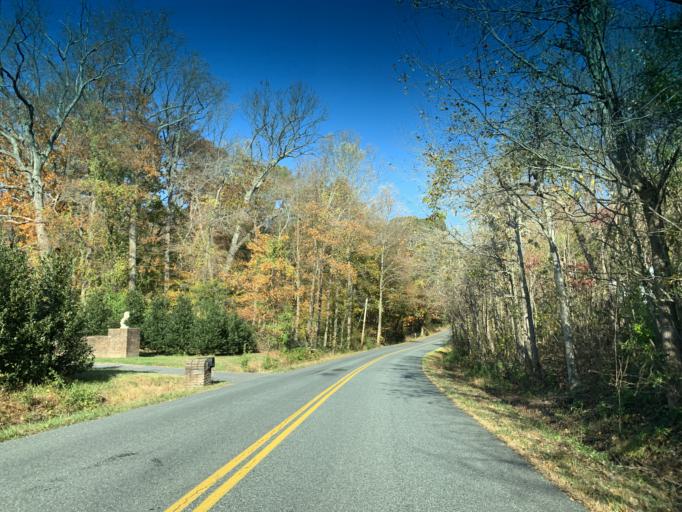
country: US
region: Maryland
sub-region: Harford County
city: Joppatowne
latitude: 39.4760
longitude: -76.3571
